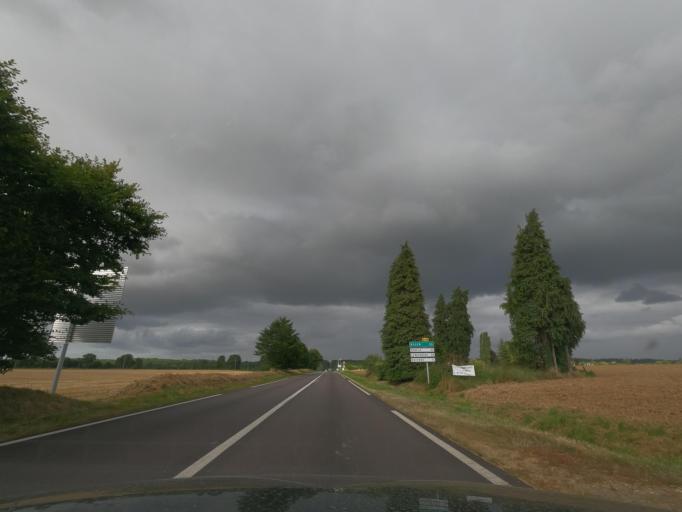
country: FR
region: Haute-Normandie
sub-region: Departement de l'Eure
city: Menneval
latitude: 49.1162
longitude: 0.6234
